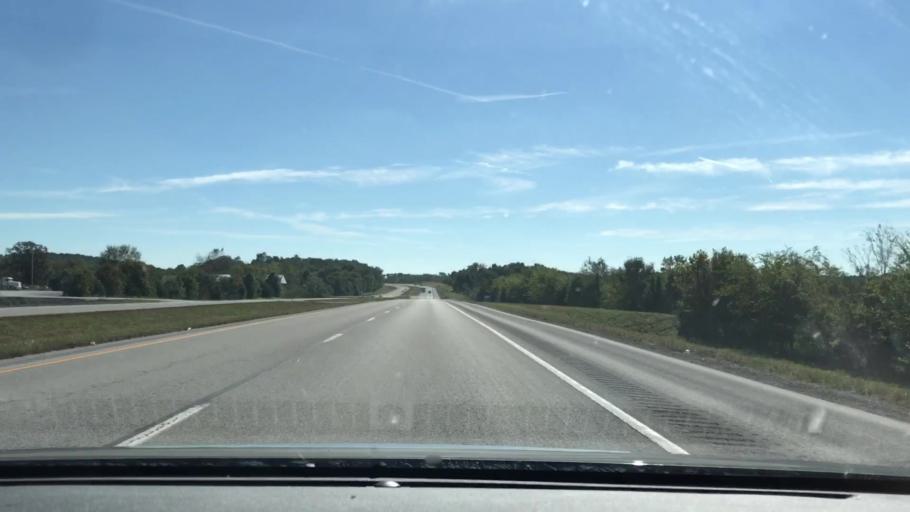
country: US
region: Kentucky
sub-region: Todd County
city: Elkton
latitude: 36.8324
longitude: -87.2309
